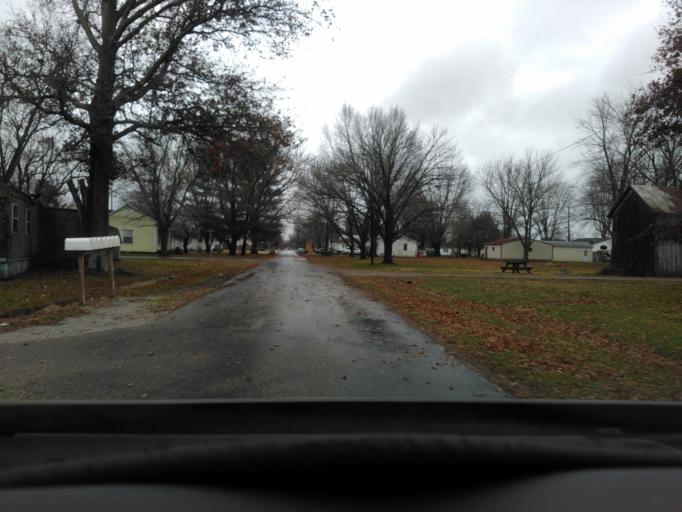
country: US
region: Illinois
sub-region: Effingham County
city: Altamont
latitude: 39.0652
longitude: -88.7554
